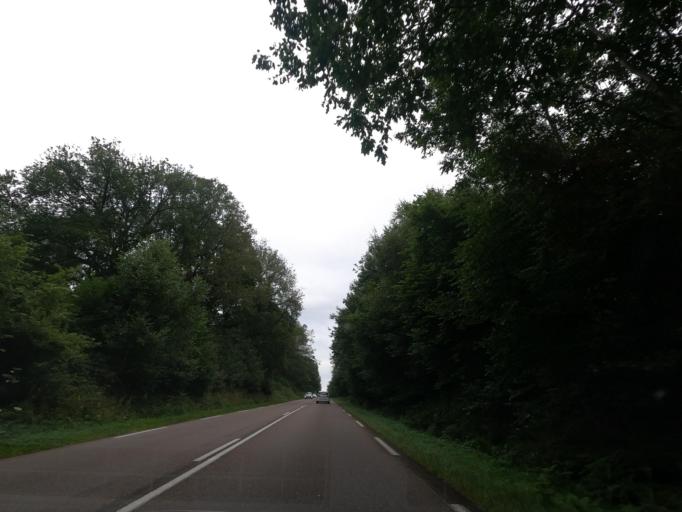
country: FR
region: Haute-Normandie
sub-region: Departement de l'Eure
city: Bourgtheroulde-Infreville
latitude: 49.2792
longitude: 0.8314
